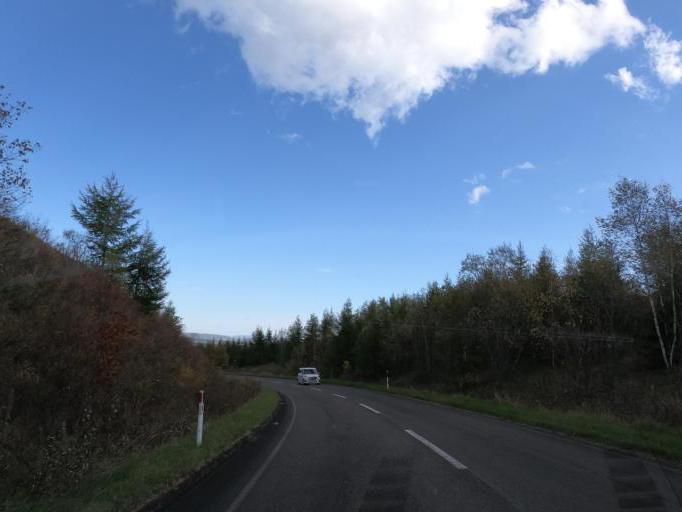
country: JP
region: Hokkaido
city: Otofuke
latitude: 43.2767
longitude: 143.2355
